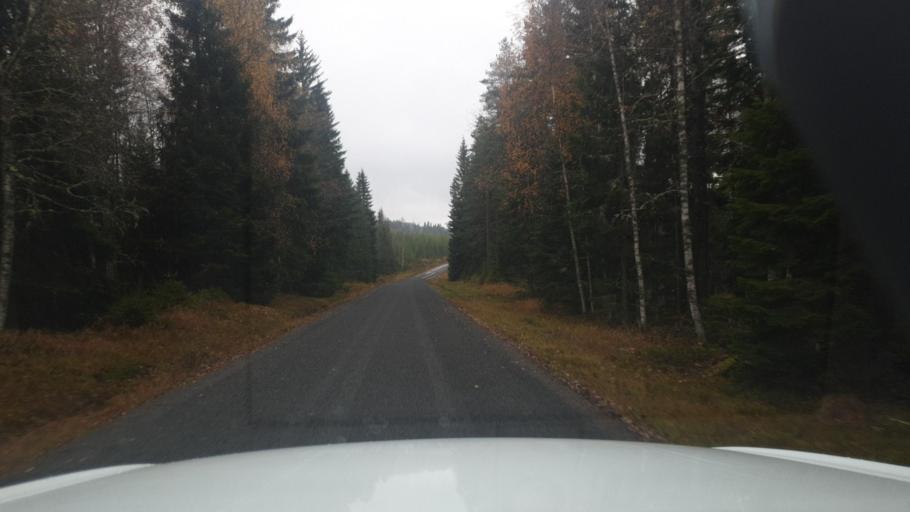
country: SE
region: Vaermland
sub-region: Eda Kommun
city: Charlottenberg
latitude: 60.1169
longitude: 12.6024
